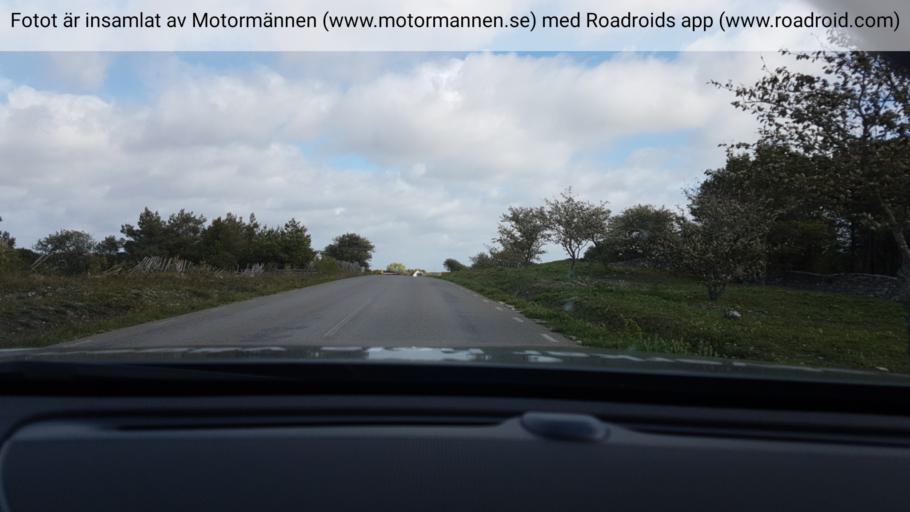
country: SE
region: Gotland
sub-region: Gotland
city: Slite
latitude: 57.9289
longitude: 19.1495
